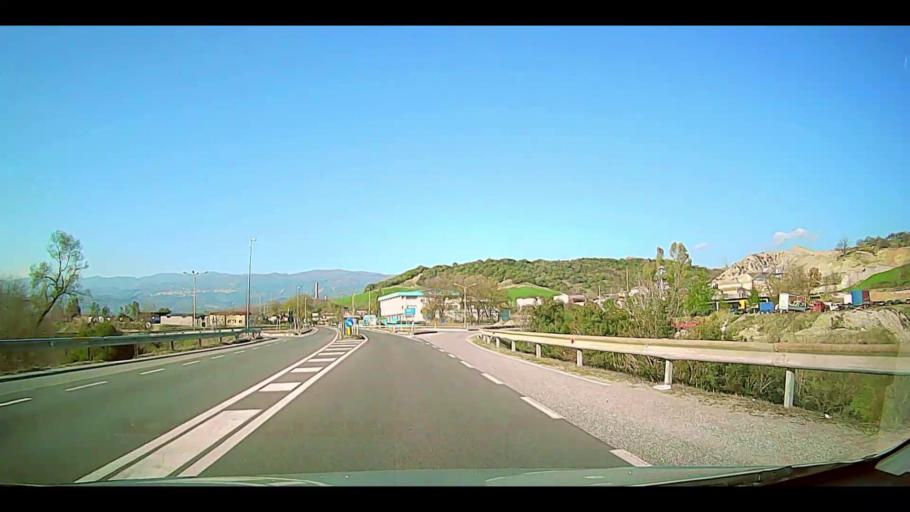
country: IT
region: Calabria
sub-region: Provincia di Crotone
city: Belvedere Spinello
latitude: 39.1887
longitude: 16.8483
